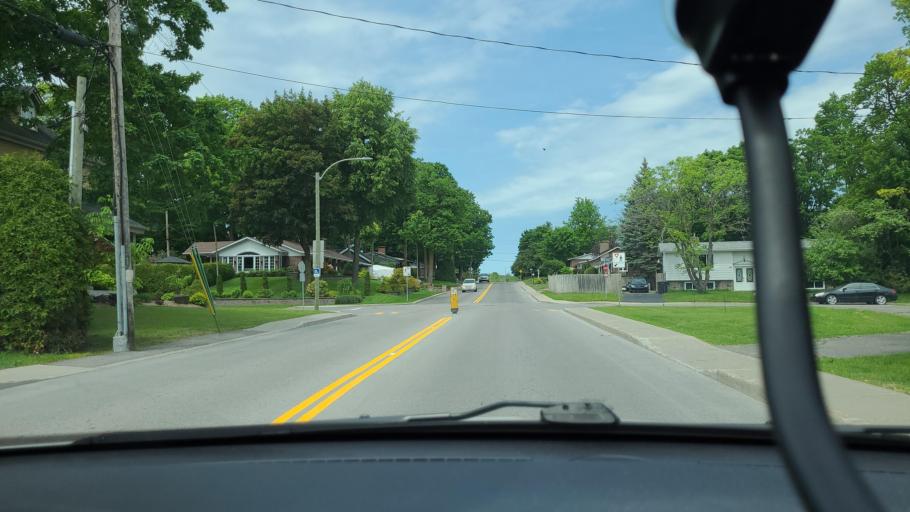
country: CA
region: Quebec
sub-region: Lanaudiere
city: Crabtree
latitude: 45.9680
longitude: -73.4789
